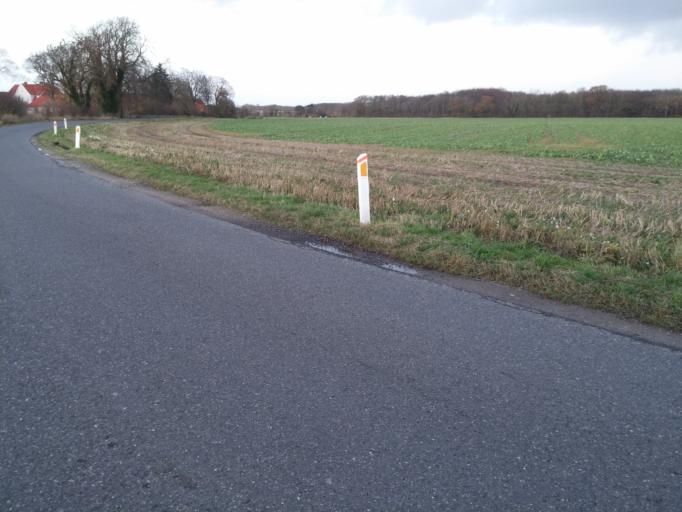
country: DK
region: South Denmark
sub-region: Kerteminde Kommune
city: Munkebo
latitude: 55.4130
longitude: 10.5590
